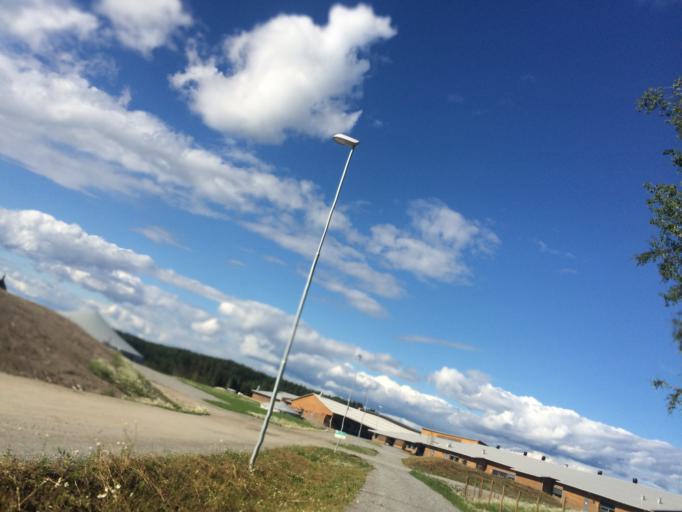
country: NO
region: Akershus
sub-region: As
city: As
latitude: 59.6753
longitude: 10.7628
